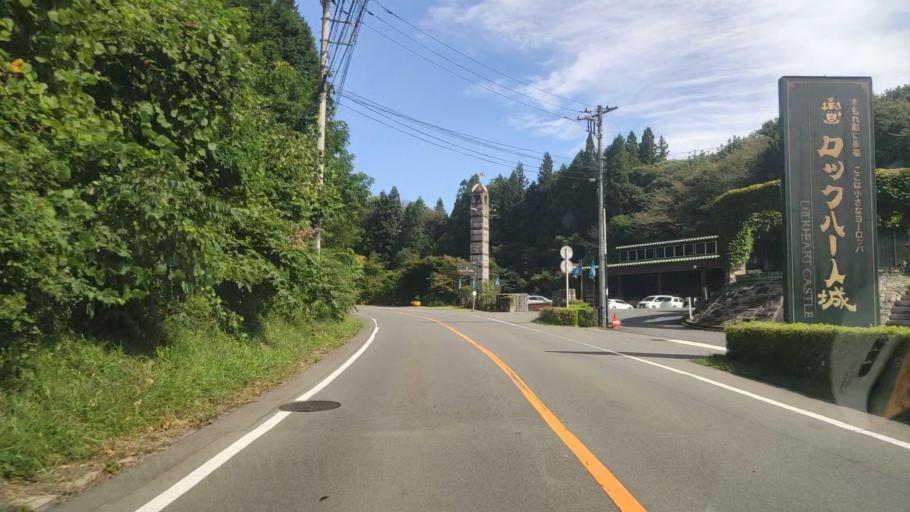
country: JP
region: Gunma
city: Numata
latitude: 36.6319
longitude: 138.9878
